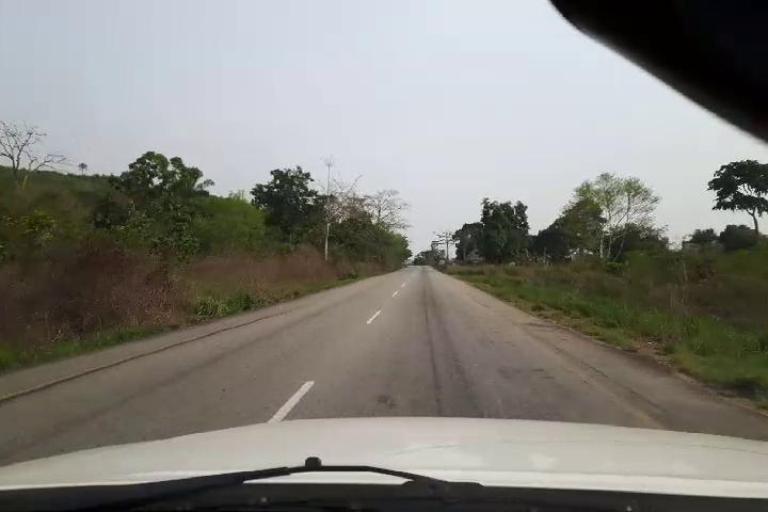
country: SL
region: Southern Province
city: Bo
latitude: 8.0080
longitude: -11.7768
